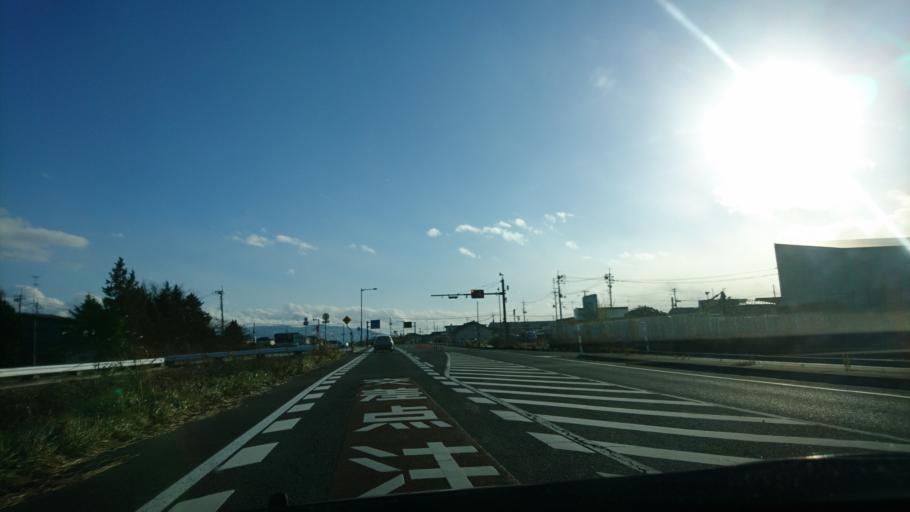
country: JP
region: Iwate
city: Mizusawa
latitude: 39.1380
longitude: 141.1627
